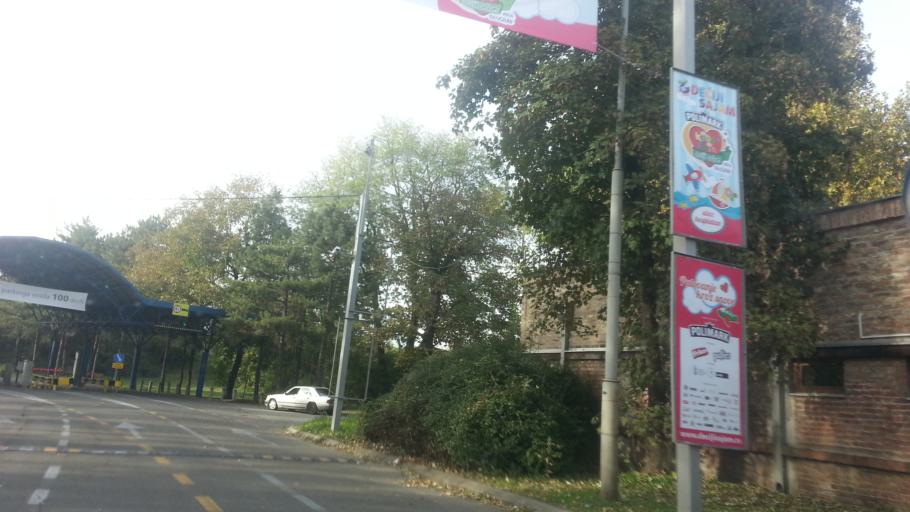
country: RS
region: Central Serbia
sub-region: Belgrade
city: Novi Beograd
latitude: 44.7984
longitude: 20.4422
